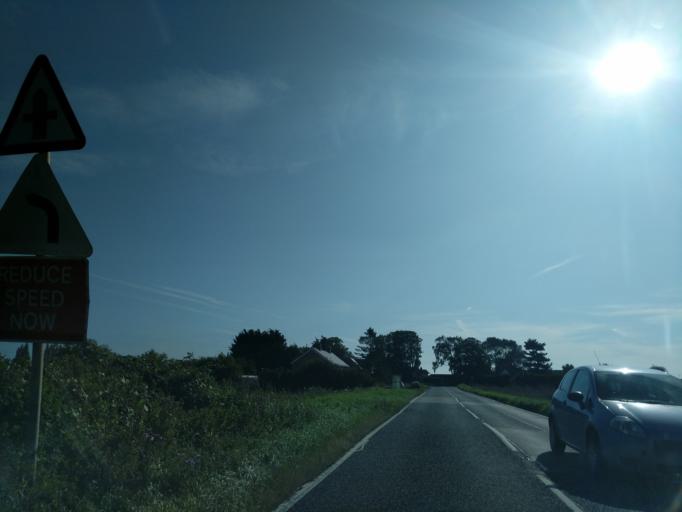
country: GB
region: England
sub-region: Lincolnshire
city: Langtoft
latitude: 52.7720
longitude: -0.2935
